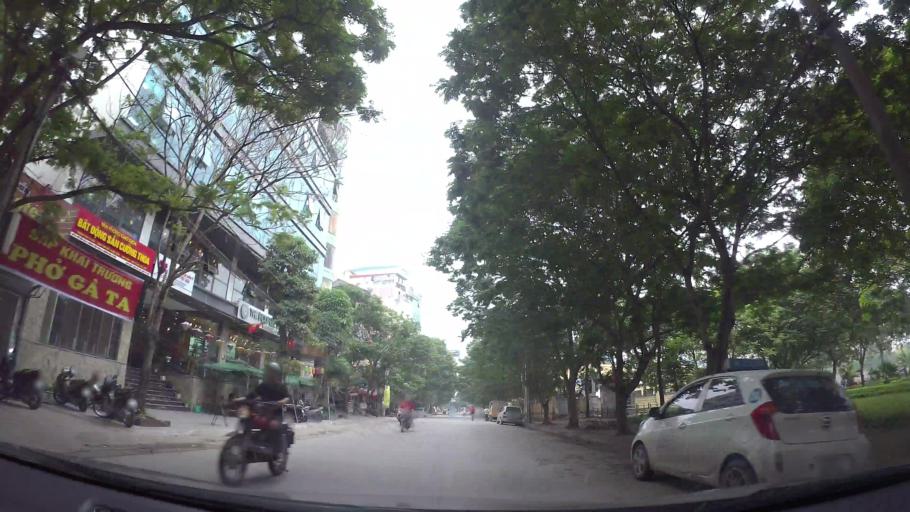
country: VN
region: Ha Noi
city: Hai BaTrung
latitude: 20.9862
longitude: 105.8561
